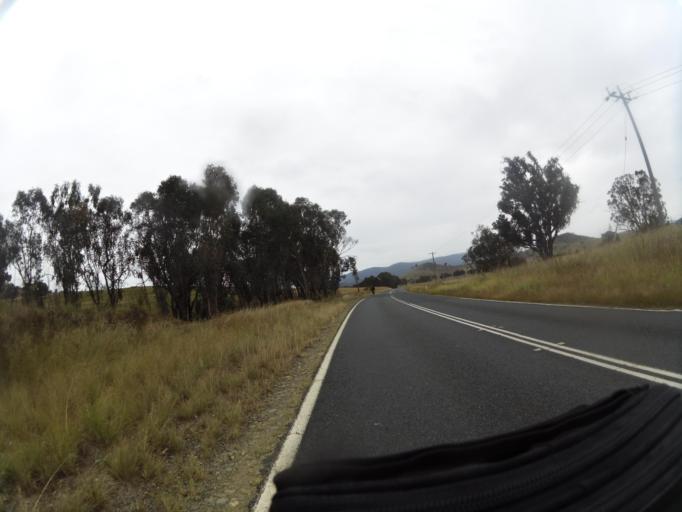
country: AU
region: New South Wales
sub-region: Greater Hume Shire
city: Holbrook
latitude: -36.2137
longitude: 147.8196
